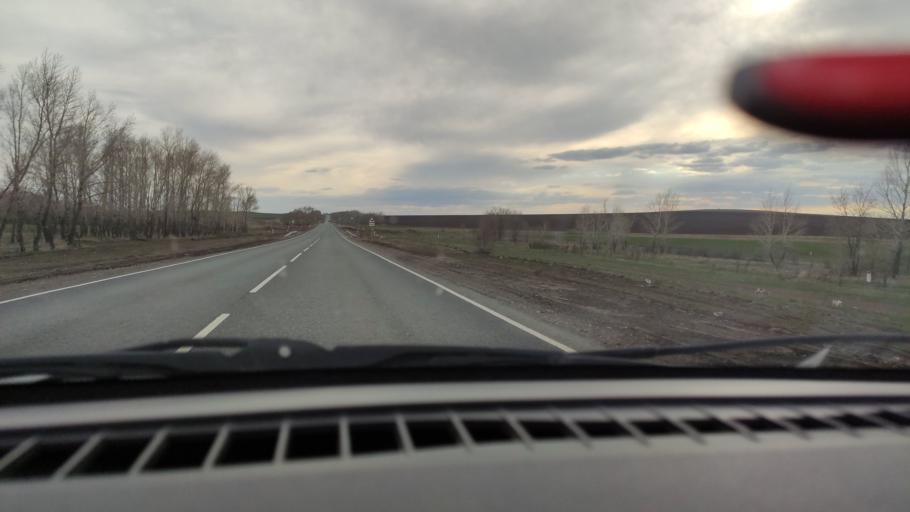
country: RU
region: Orenburg
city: Sakmara
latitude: 52.3143
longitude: 55.4646
